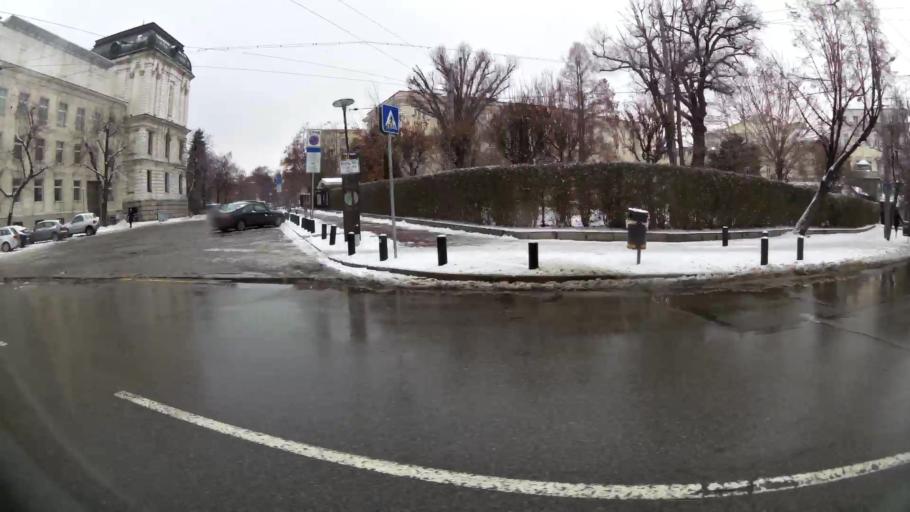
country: BG
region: Sofia-Capital
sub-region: Stolichna Obshtina
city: Sofia
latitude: 42.6968
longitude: 23.3350
